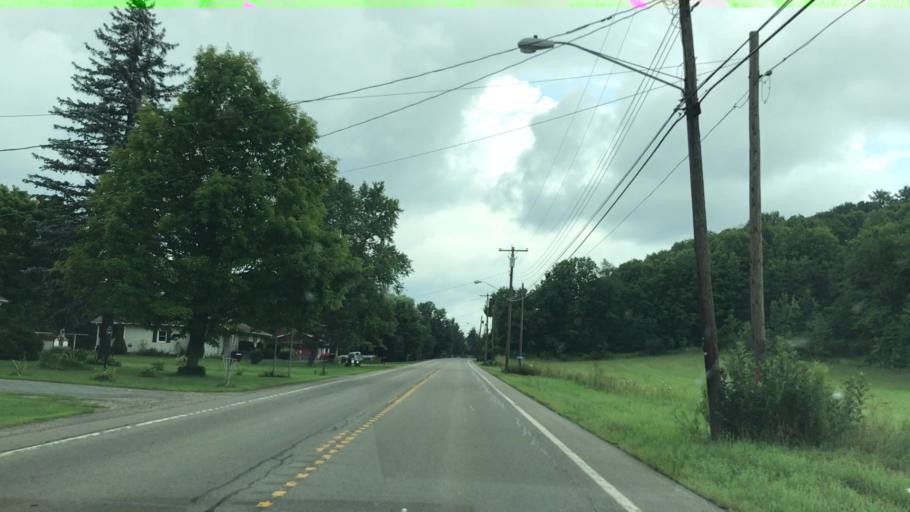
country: US
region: New York
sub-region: Steuben County
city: Bath
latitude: 42.3809
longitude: -77.3609
